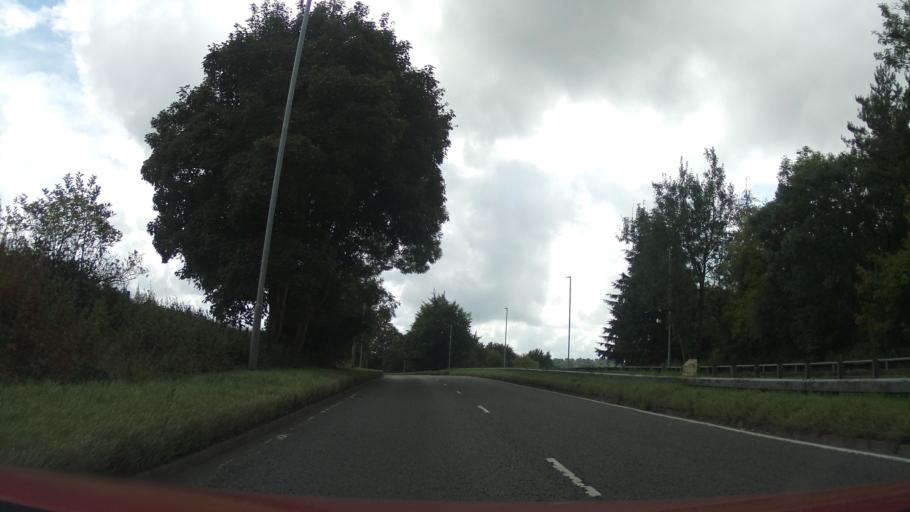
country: GB
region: England
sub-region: Staffordshire
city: Barlaston
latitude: 52.9594
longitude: -2.1939
